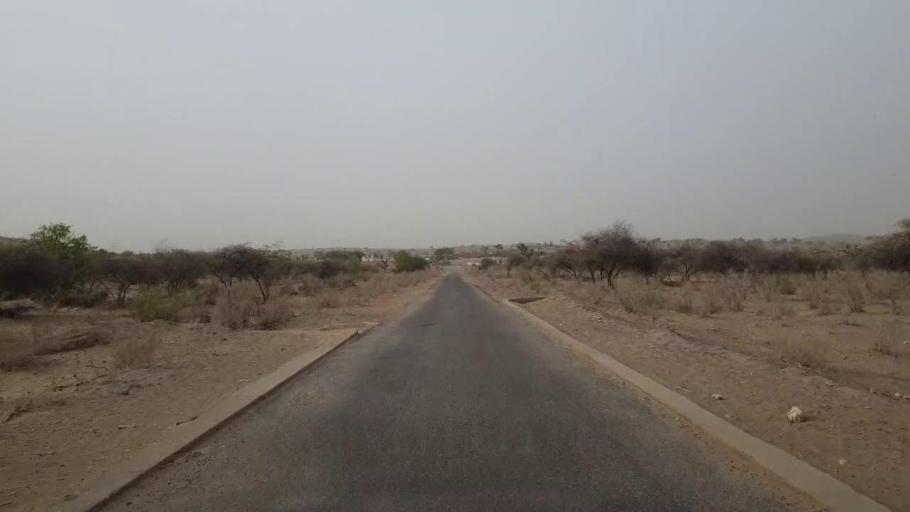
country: PK
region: Sindh
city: Islamkot
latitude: 24.5708
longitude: 70.3646
